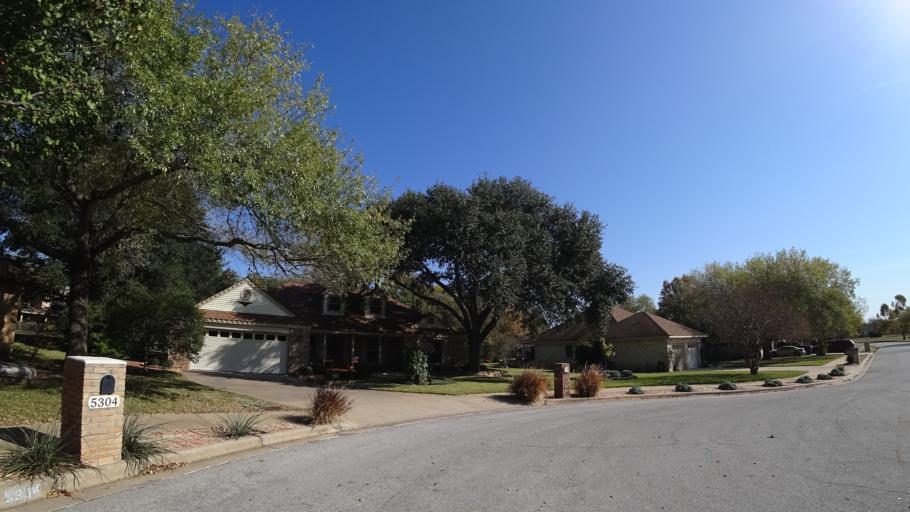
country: US
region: Texas
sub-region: Travis County
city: Shady Hollow
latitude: 30.2230
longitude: -97.8550
